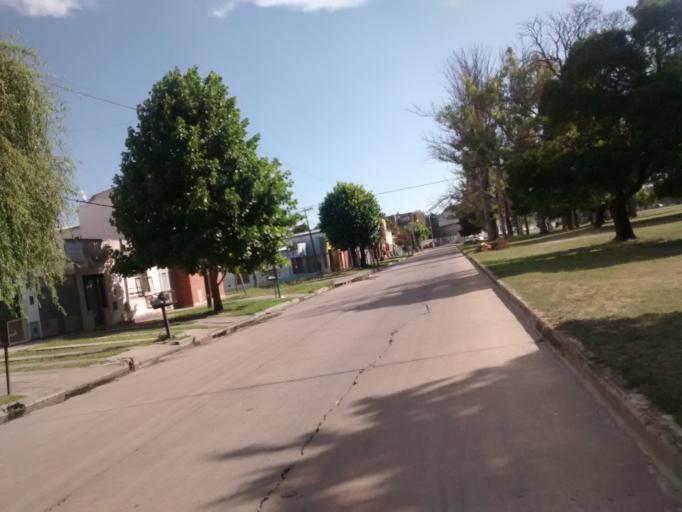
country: AR
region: Buenos Aires
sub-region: Partido de La Plata
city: La Plata
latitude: -34.9527
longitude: -57.9506
